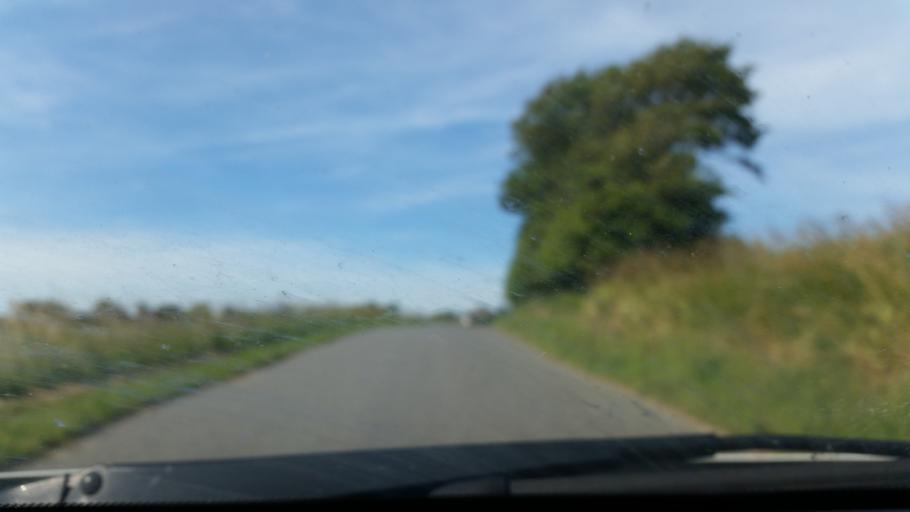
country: DK
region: Central Jutland
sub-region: Samso Kommune
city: Tranebjerg
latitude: 55.7911
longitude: 10.5560
